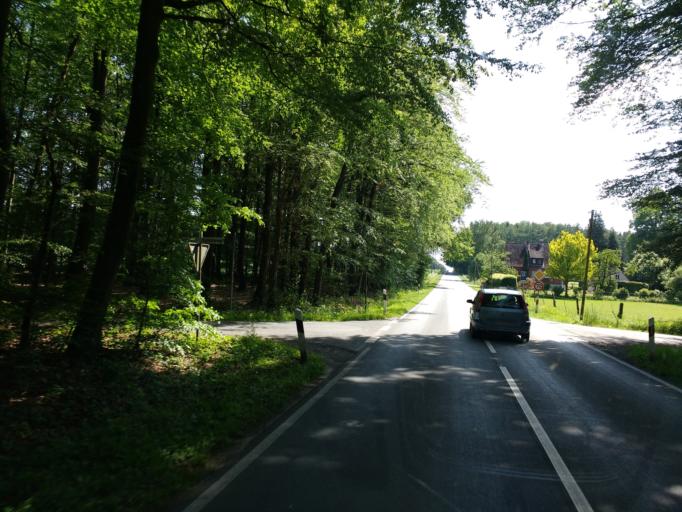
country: DE
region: Lower Saxony
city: Belm
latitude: 52.3209
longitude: 8.1116
